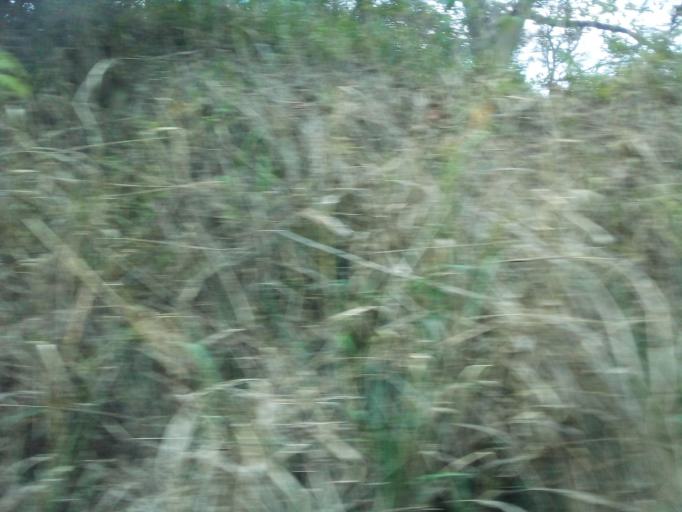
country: BR
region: Minas Gerais
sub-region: Belo Horizonte
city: Belo Horizonte
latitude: -19.8725
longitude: -43.8506
